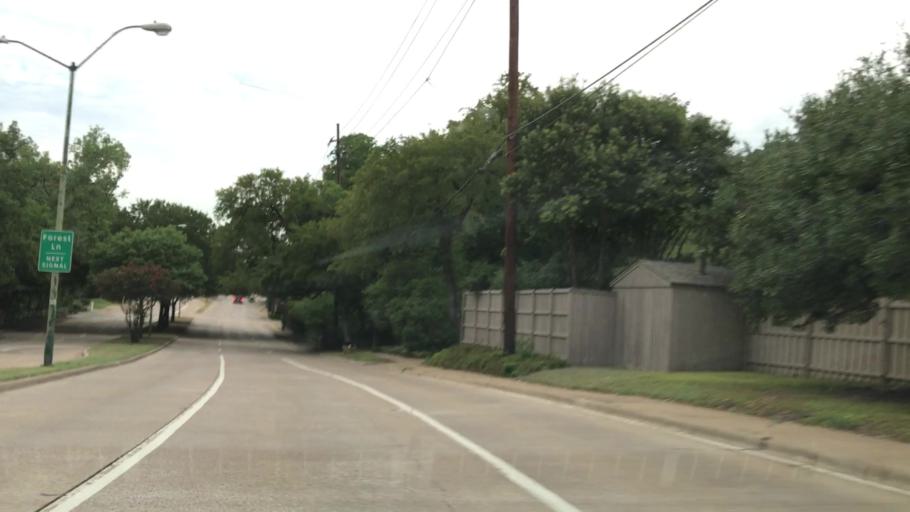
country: US
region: Texas
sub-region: Dallas County
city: University Park
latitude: 32.9067
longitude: -96.7864
